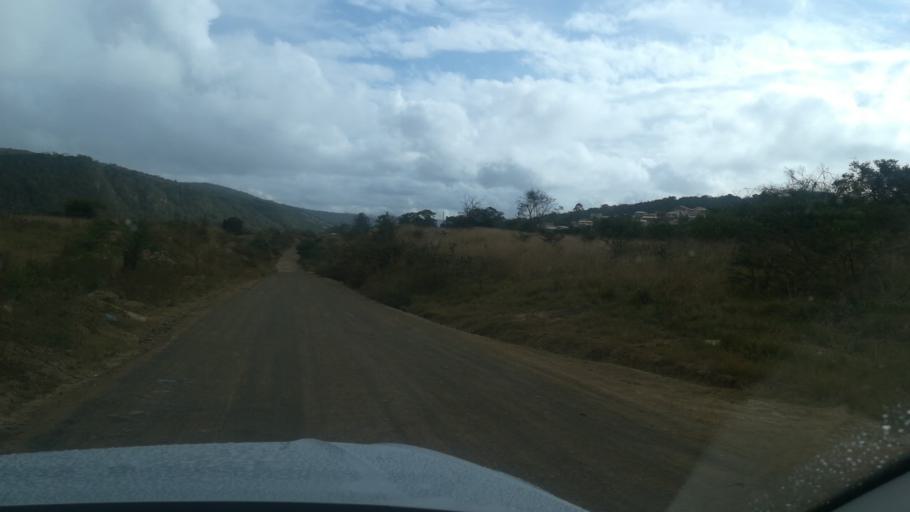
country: ZA
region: Eastern Cape
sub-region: Buffalo City Metropolitan Municipality
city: East London
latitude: -32.9961
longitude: 27.8018
